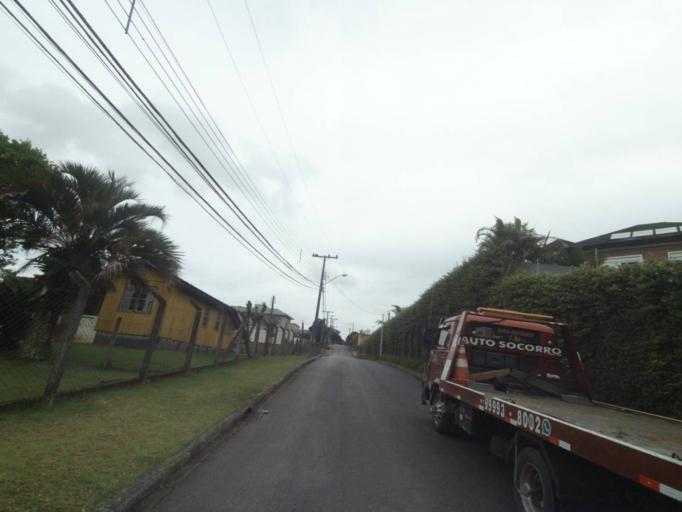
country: BR
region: Parana
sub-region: Curitiba
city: Curitiba
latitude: -25.4501
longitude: -49.3349
